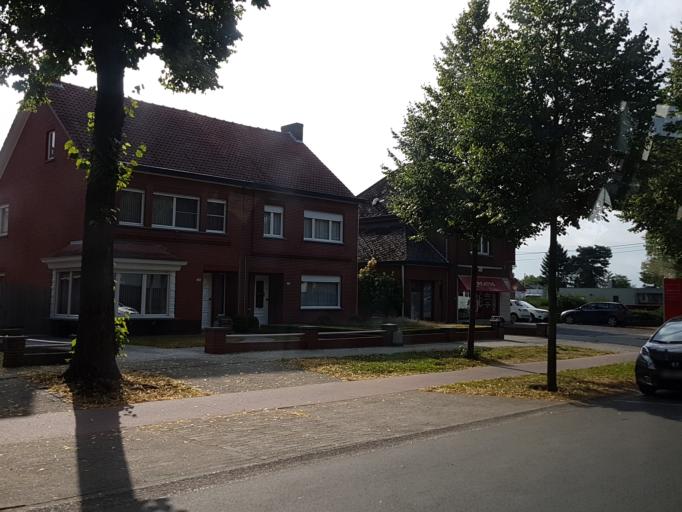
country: BE
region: Flanders
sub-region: Provincie Antwerpen
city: Westerlo
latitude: 51.0963
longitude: 4.9113
